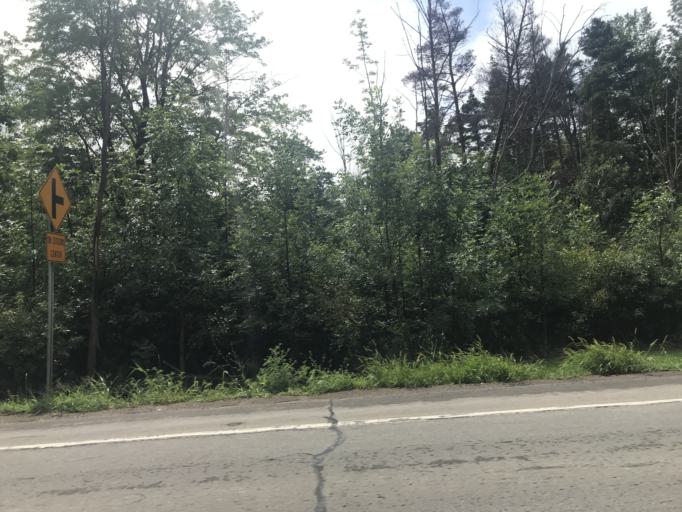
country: US
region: New York
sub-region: Chautauqua County
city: Silver Creek
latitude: 42.5458
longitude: -79.1821
